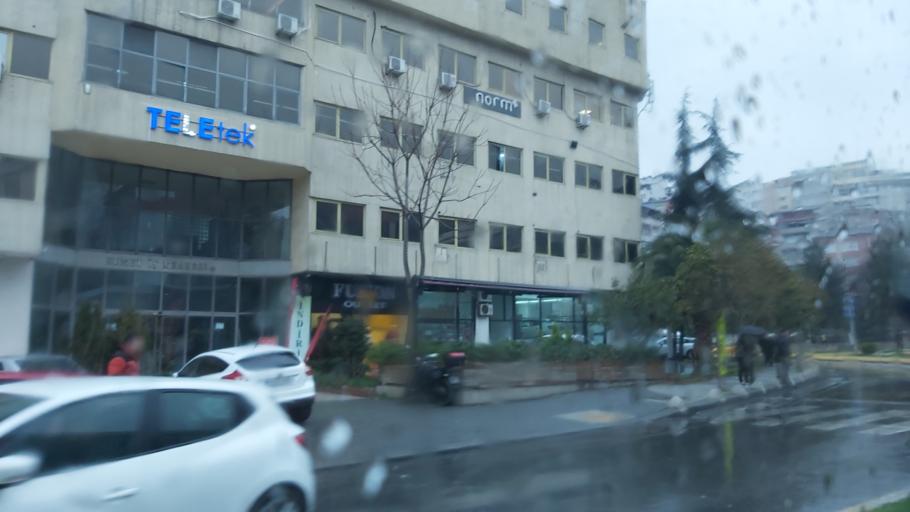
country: TR
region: Istanbul
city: Sisli
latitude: 41.0840
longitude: 28.9847
